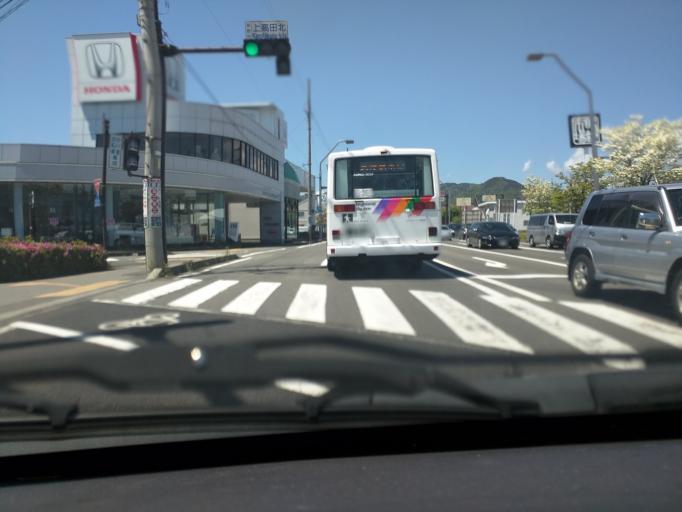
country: JP
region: Nagano
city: Nagano-shi
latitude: 36.6417
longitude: 138.2143
